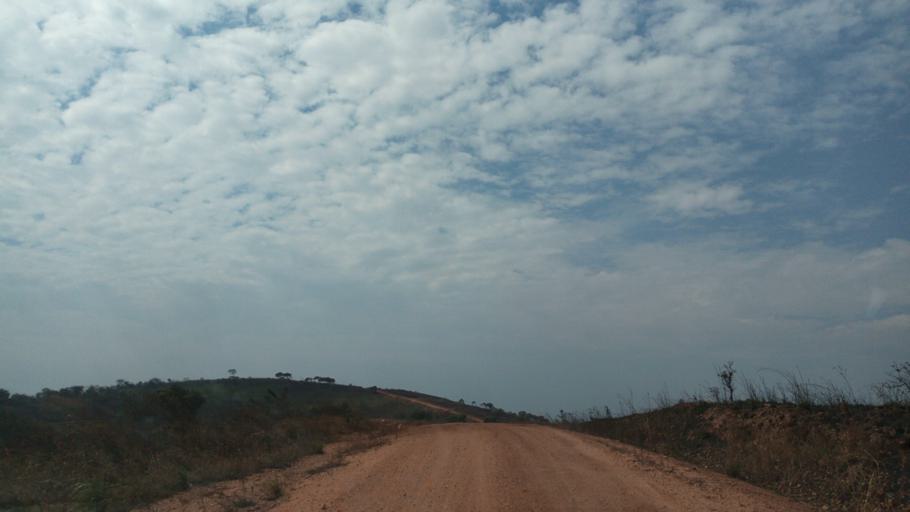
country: CD
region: Katanga
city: Kalemie
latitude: -6.2128
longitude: 28.9065
